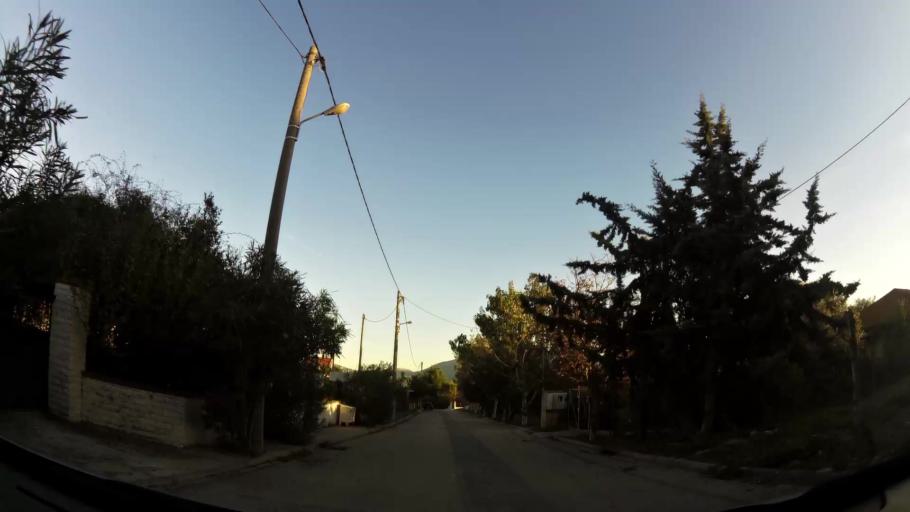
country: GR
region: Attica
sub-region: Nomarchia Anatolikis Attikis
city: Kryoneri
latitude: 38.1425
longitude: 23.8312
